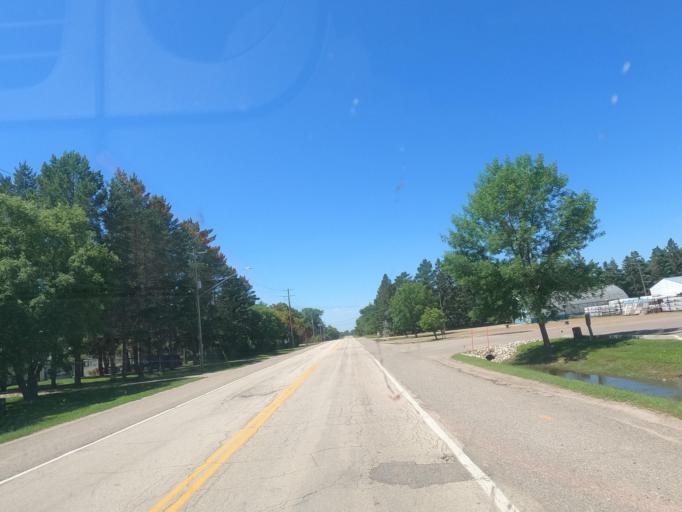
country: CA
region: Manitoba
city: Souris
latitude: 49.6211
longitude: -100.2700
